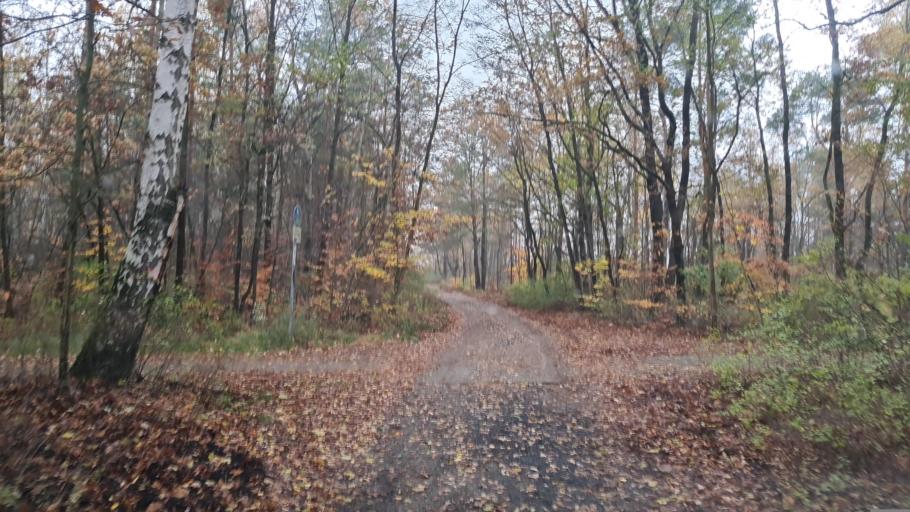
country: DE
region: Brandenburg
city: Lauchhammer
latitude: 51.5006
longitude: 13.7863
